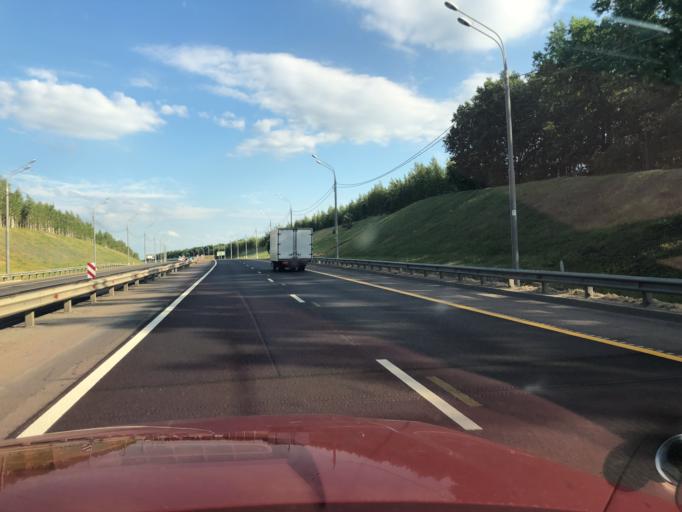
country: RU
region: Lipetsk
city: Zadonsk
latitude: 52.3917
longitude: 38.8635
